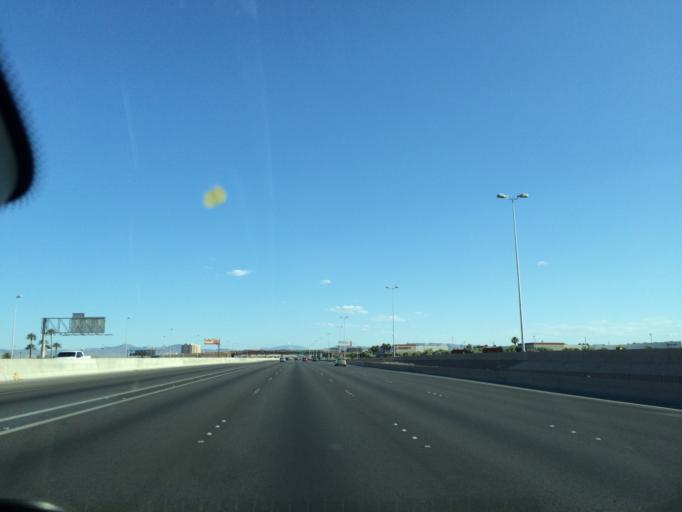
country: US
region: Nevada
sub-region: Clark County
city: Paradise
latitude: 36.0630
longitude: -115.1809
